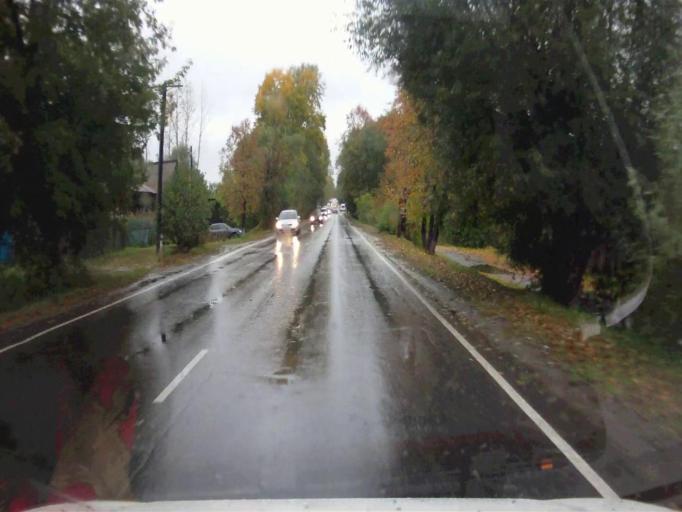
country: RU
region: Chelyabinsk
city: Kyshtym
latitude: 55.7175
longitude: 60.5421
